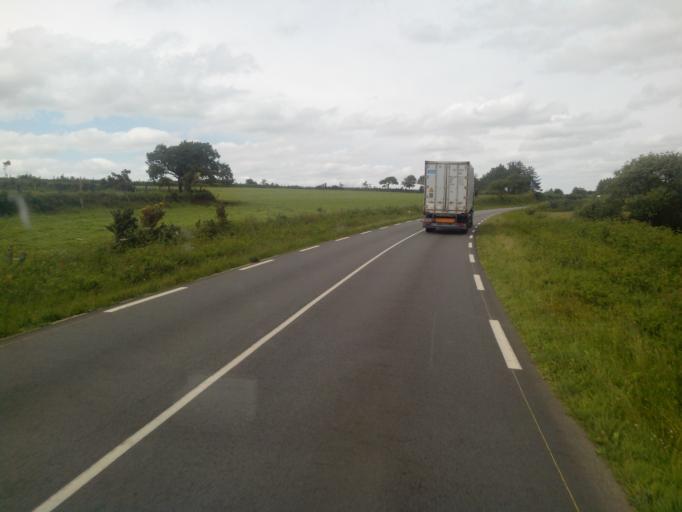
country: FR
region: Brittany
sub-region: Departement du Finistere
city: Guerlesquin
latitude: 48.5433
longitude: -3.6012
